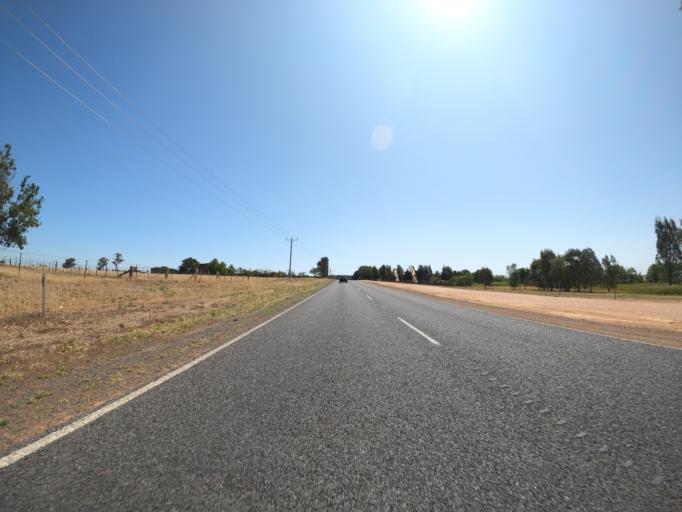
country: AU
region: Victoria
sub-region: Moira
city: Yarrawonga
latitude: -36.0273
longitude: 146.0794
